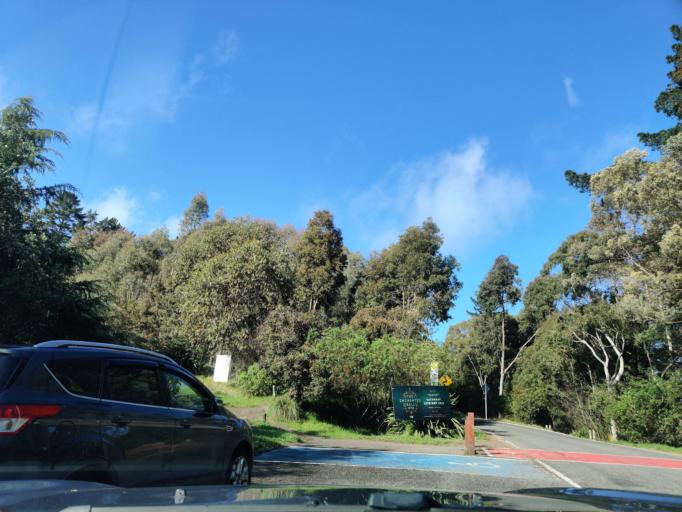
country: NZ
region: Hawke's Bay
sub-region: Hastings District
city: Hastings
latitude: -39.6952
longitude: 176.9017
